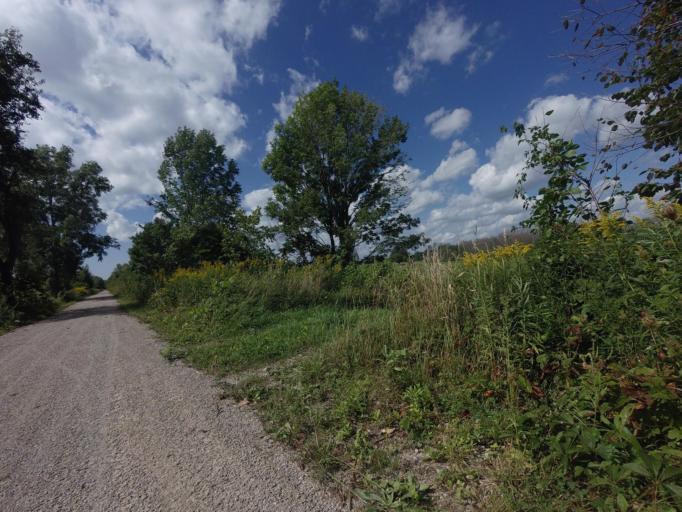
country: CA
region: Ontario
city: Huron East
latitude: 43.7201
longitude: -81.3966
